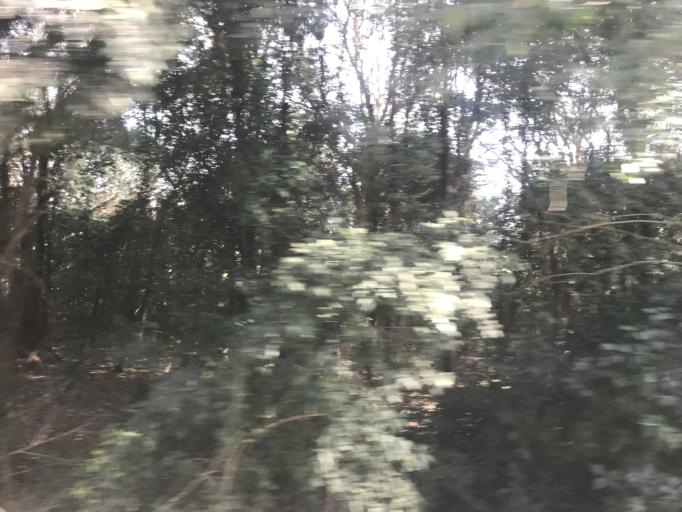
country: AR
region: Cordoba
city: Laguna Larga
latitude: -31.7968
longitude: -63.7857
